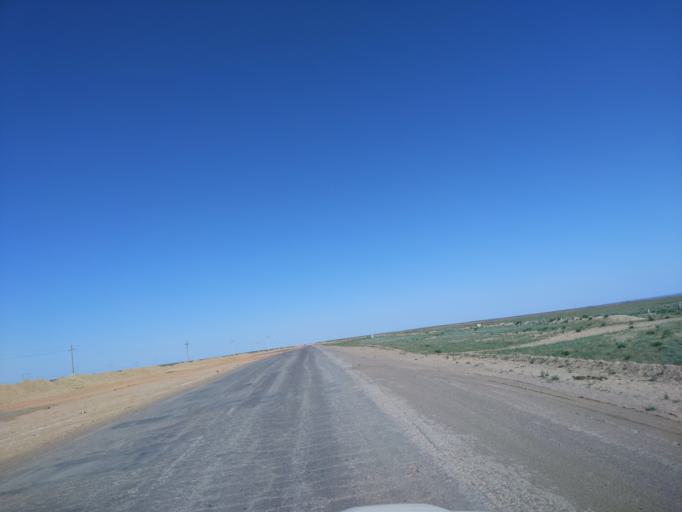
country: KZ
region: Almaty Oblysy
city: Bakanas
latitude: 44.1510
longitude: 75.8624
